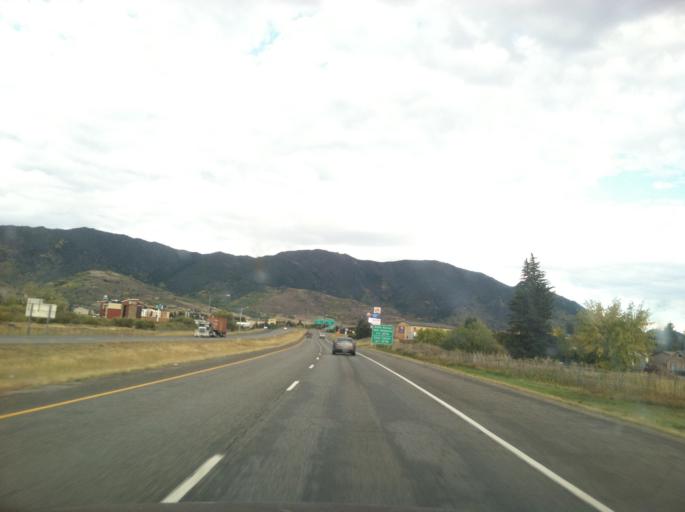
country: US
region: Montana
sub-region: Silver Bow County
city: Butte
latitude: 45.9865
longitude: -112.5164
